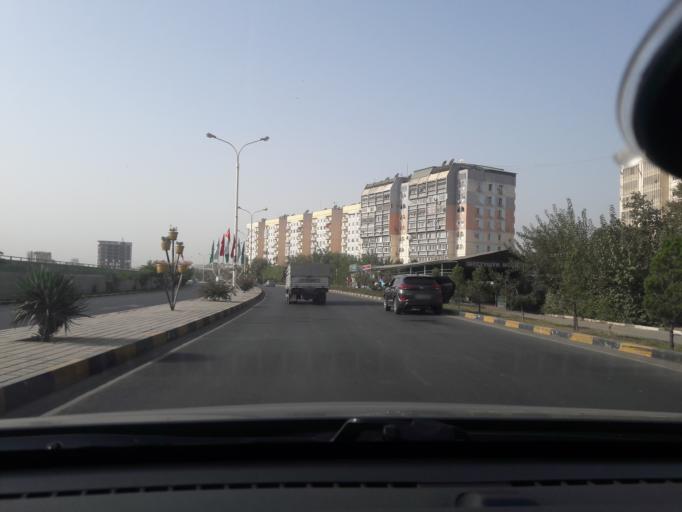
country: TJ
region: Dushanbe
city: Dushanbe
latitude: 38.5506
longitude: 68.7663
